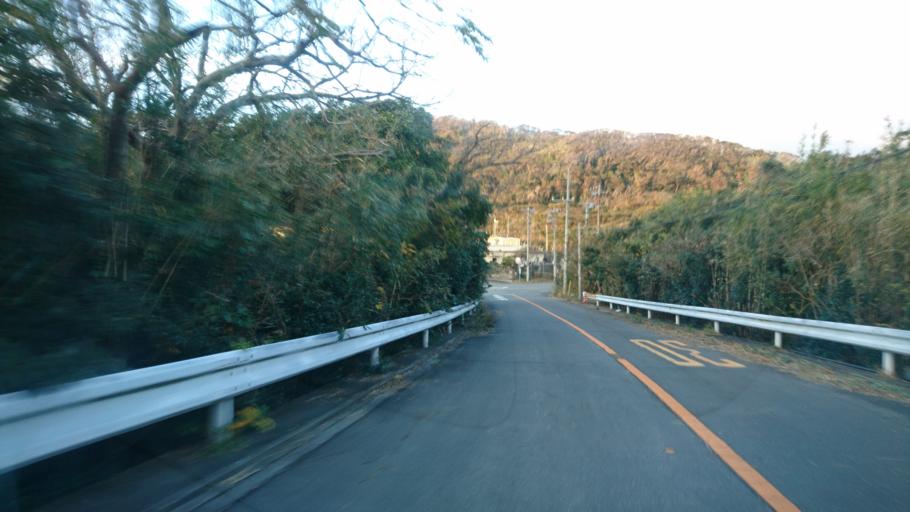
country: JP
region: Shizuoka
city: Shimoda
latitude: 34.3627
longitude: 139.2557
